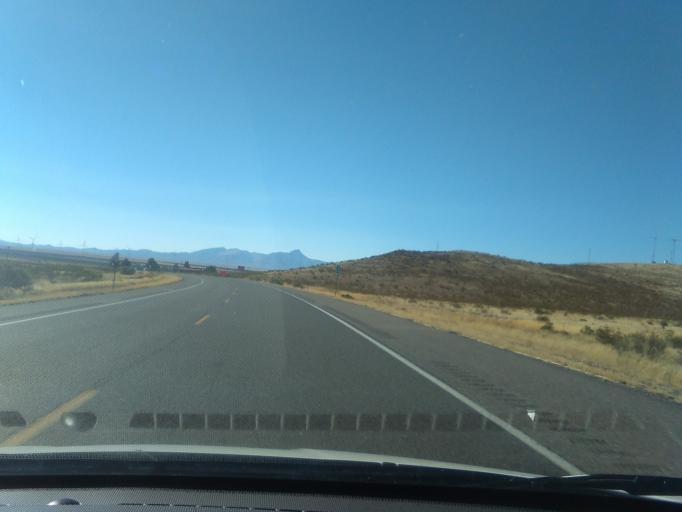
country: US
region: New Mexico
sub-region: Dona Ana County
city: Hatch
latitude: 32.5778
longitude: -107.4464
